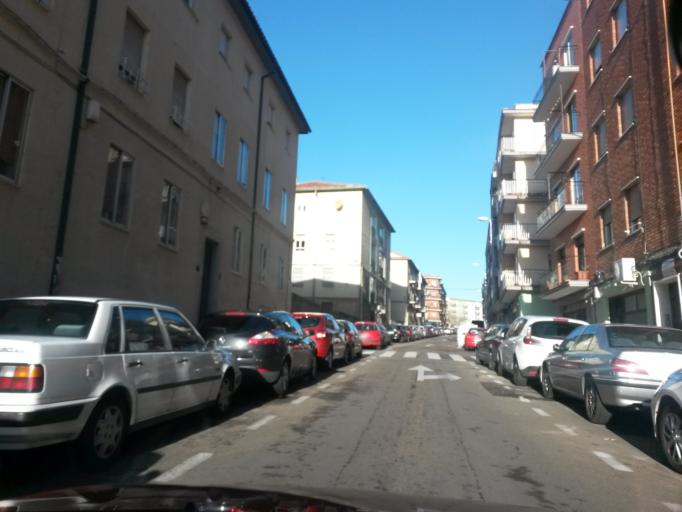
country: ES
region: Castille and Leon
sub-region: Provincia de Salamanca
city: Salamanca
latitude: 40.9746
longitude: -5.6651
